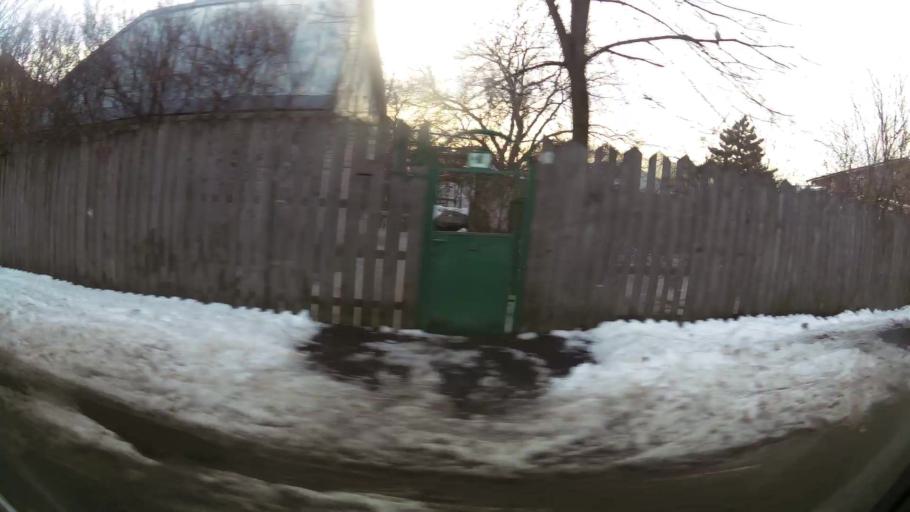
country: RO
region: Bucuresti
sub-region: Municipiul Bucuresti
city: Bucuresti
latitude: 44.3896
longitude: 26.0720
